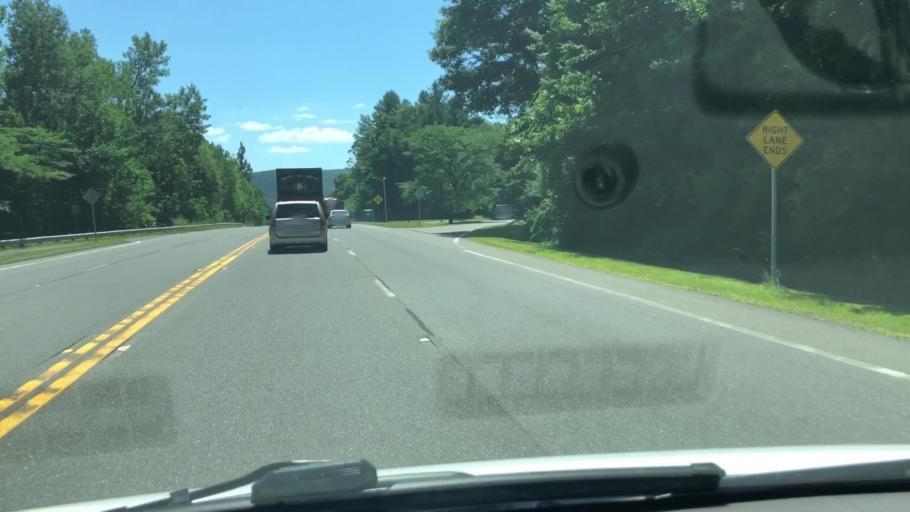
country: US
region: Massachusetts
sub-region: Berkshire County
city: Adams
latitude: 42.5888
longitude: -73.1466
